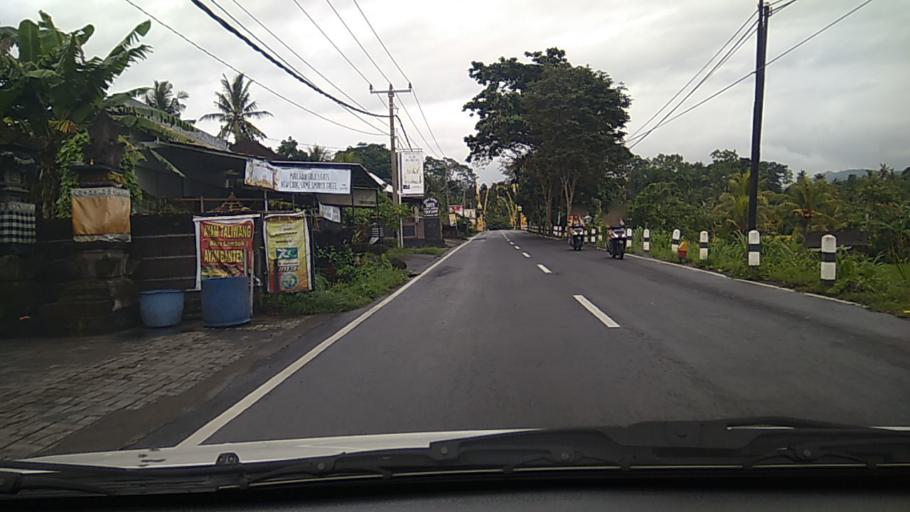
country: ID
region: Bali
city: Banjar Budakeling
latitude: -8.4275
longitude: 115.5925
